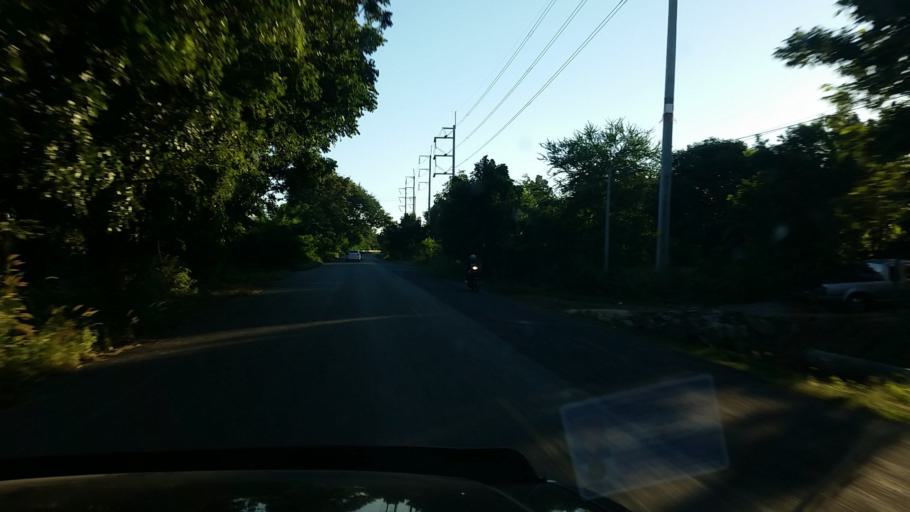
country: TH
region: Chaiyaphum
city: Sap Yai
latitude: 15.6718
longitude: 101.6745
